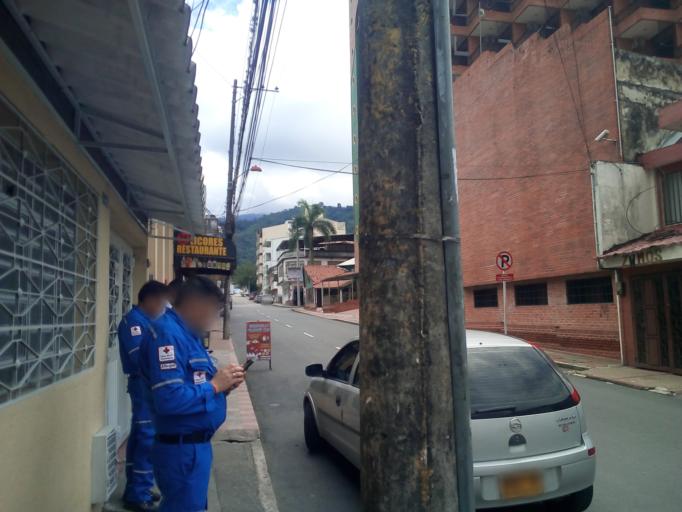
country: CO
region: Tolima
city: Ibague
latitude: 4.4486
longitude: -75.2475
